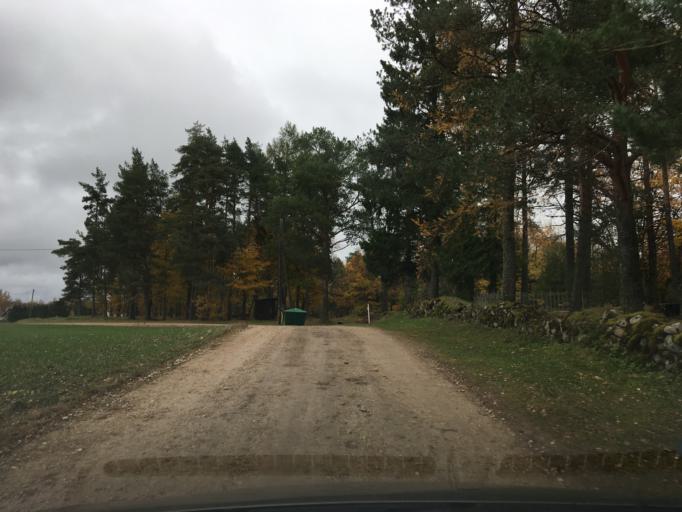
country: EE
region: Harju
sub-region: Raasiku vald
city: Raasiku
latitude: 59.1742
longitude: 25.1640
